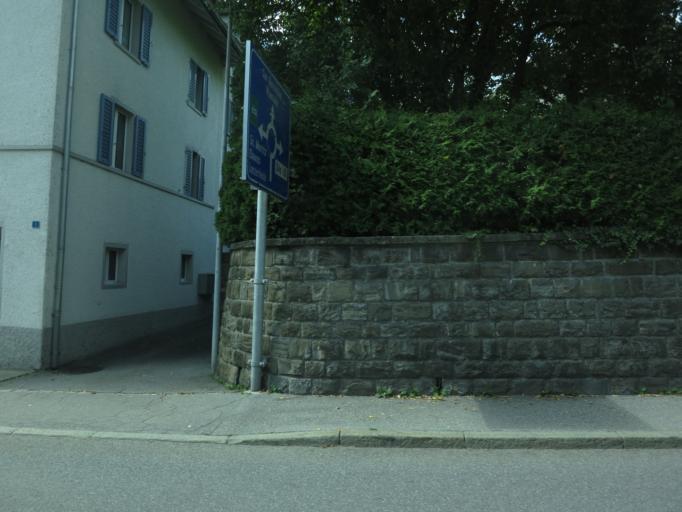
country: CH
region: Grisons
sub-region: Hinterrhein District
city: Thusis
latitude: 46.6942
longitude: 9.4395
